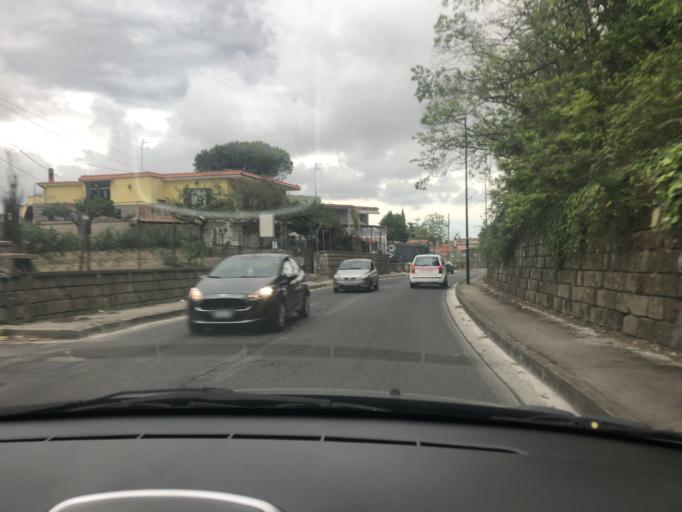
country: IT
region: Campania
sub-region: Provincia di Napoli
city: Torre Caracciolo
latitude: 40.8632
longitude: 14.2024
